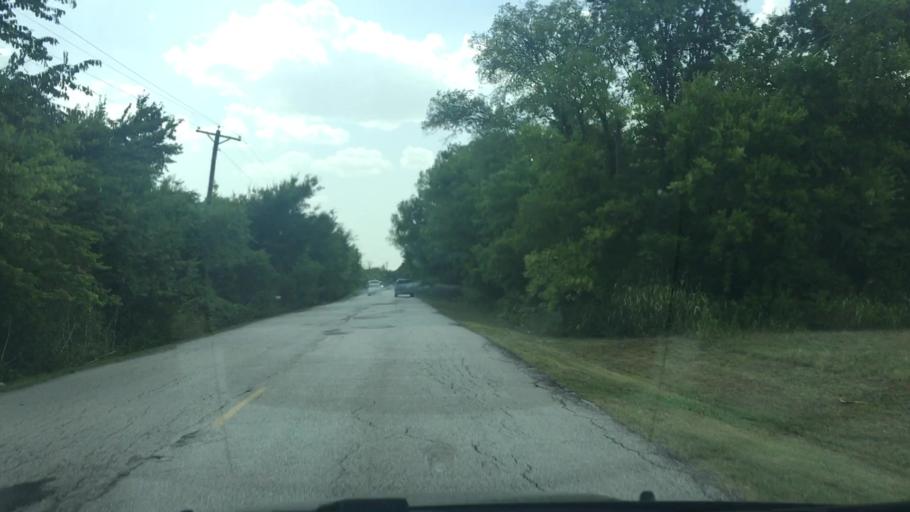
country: US
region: Texas
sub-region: Dallas County
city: Glenn Heights
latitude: 32.5607
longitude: -96.8153
